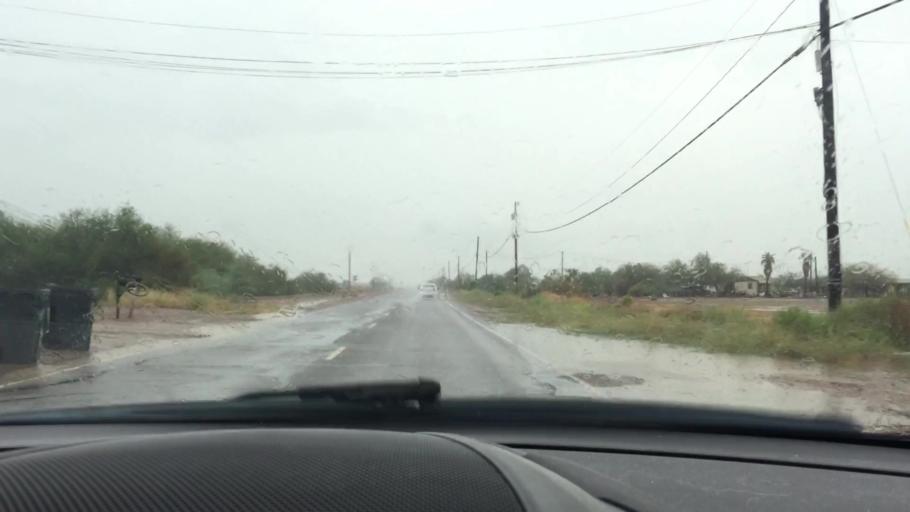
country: US
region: Arizona
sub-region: Maricopa County
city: Scottsdale
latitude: 33.4767
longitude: -111.8827
